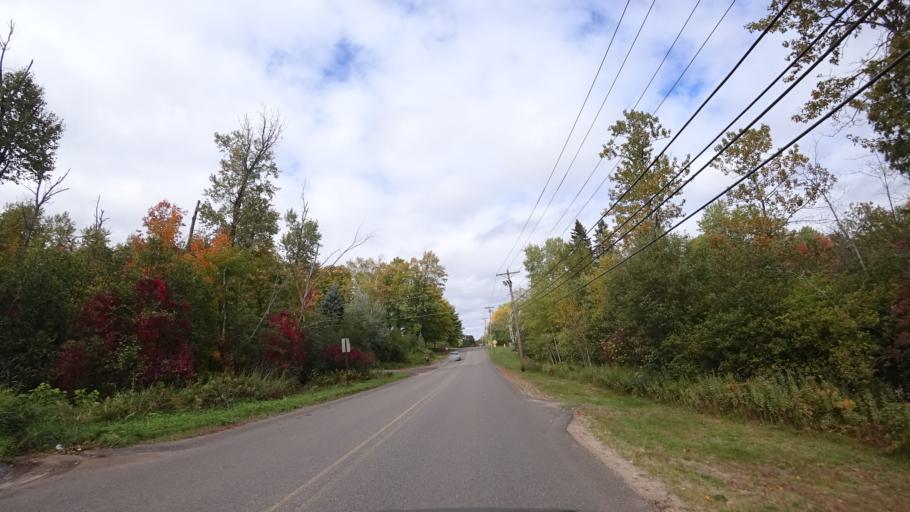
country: US
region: Michigan
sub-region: Marquette County
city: Trowbridge Park
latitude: 46.5451
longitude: -87.4374
